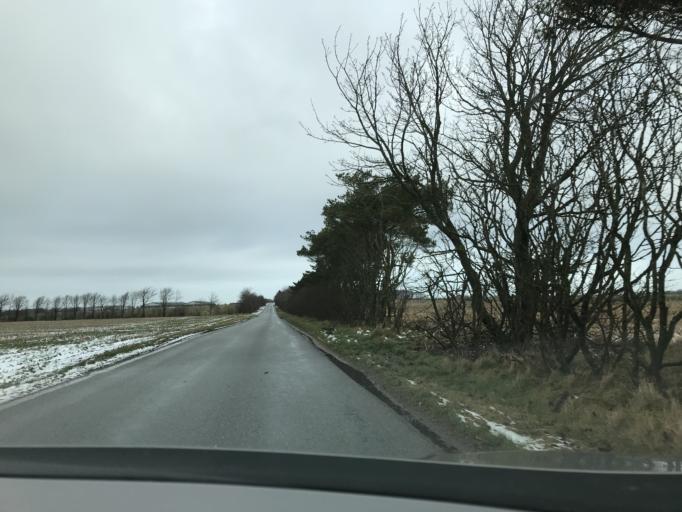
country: DK
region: South Denmark
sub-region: Varde Kommune
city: Varde
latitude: 55.6510
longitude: 8.4116
